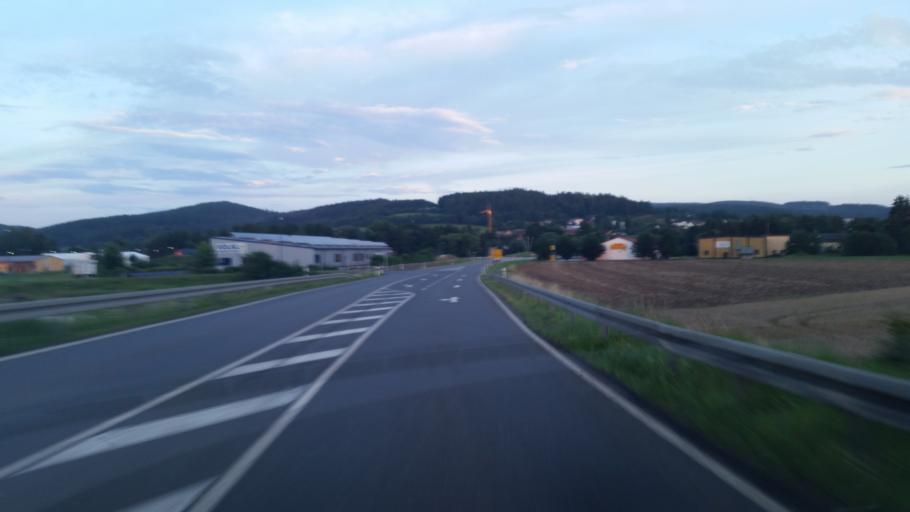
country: DE
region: Bavaria
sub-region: Upper Palatinate
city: Luhe-Wildenau
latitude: 49.5910
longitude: 12.1447
